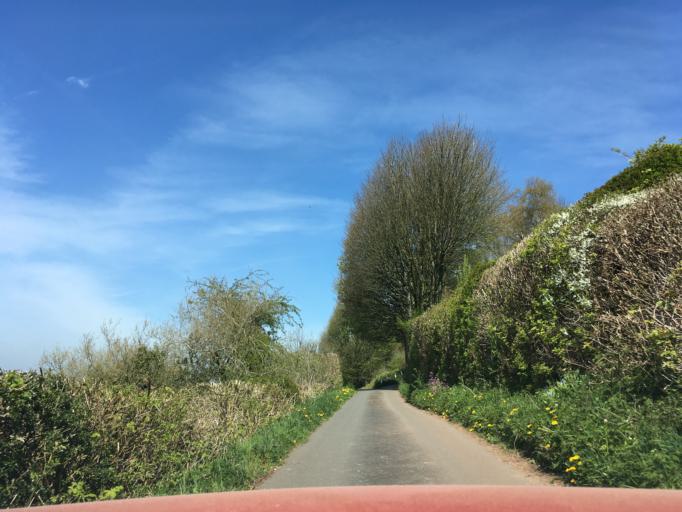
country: GB
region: Wales
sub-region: Monmouthshire
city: Llangwm
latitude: 51.6828
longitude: -2.8115
